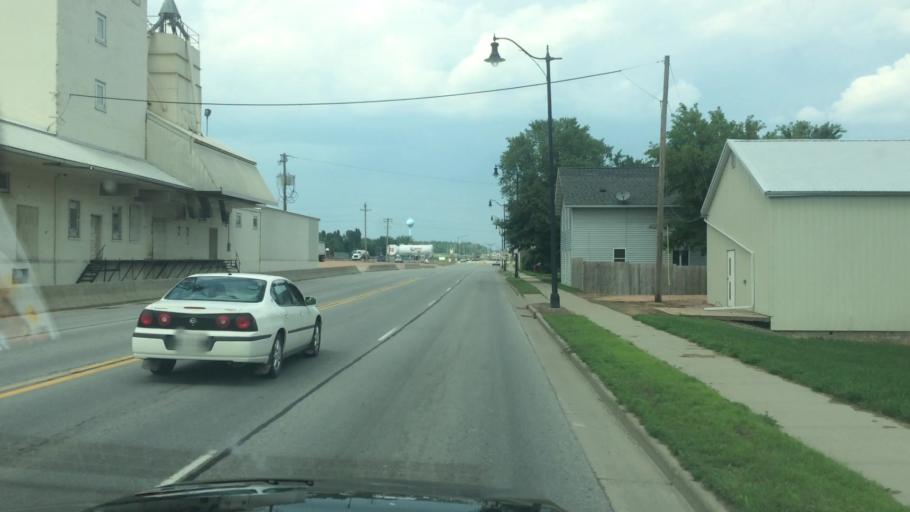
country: US
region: Wisconsin
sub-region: Clark County
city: Colby
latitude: 44.9098
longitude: -90.3153
